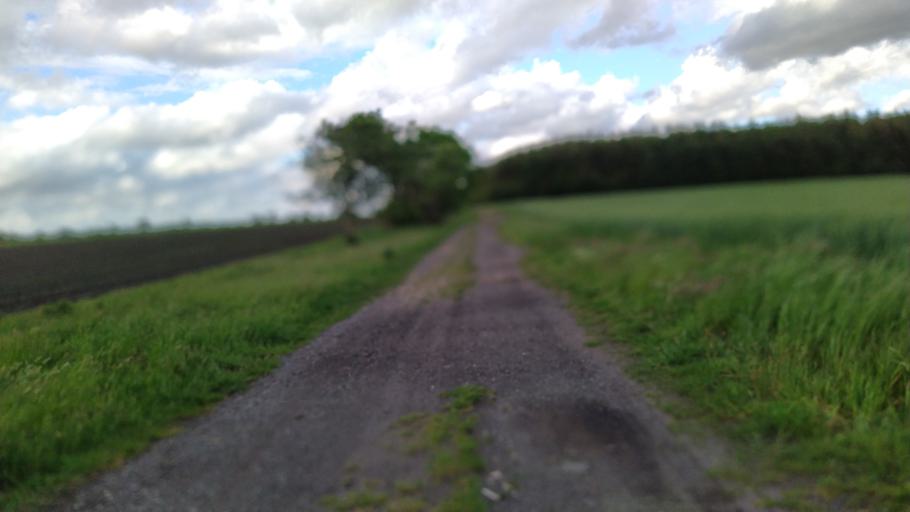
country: DE
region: Lower Saxony
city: Farven
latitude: 53.4548
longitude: 9.3016
